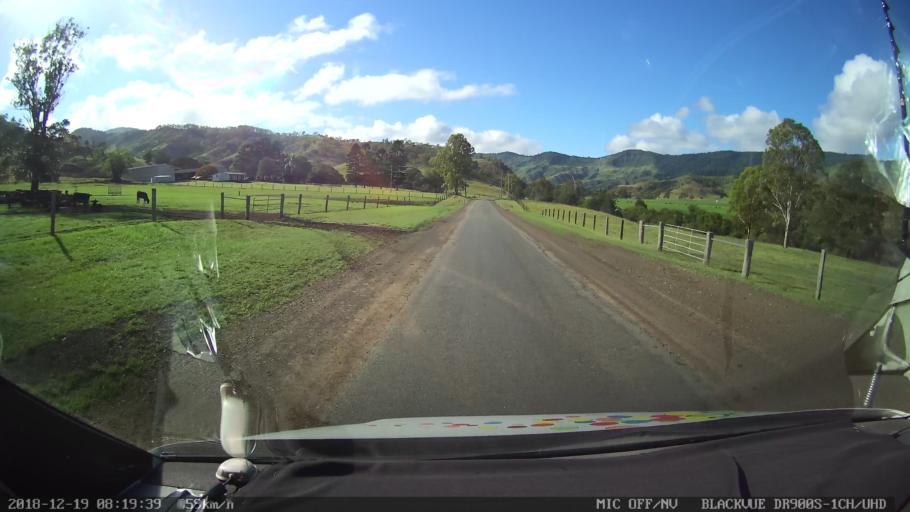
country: AU
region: New South Wales
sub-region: Kyogle
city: Kyogle
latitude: -28.2839
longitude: 152.9095
